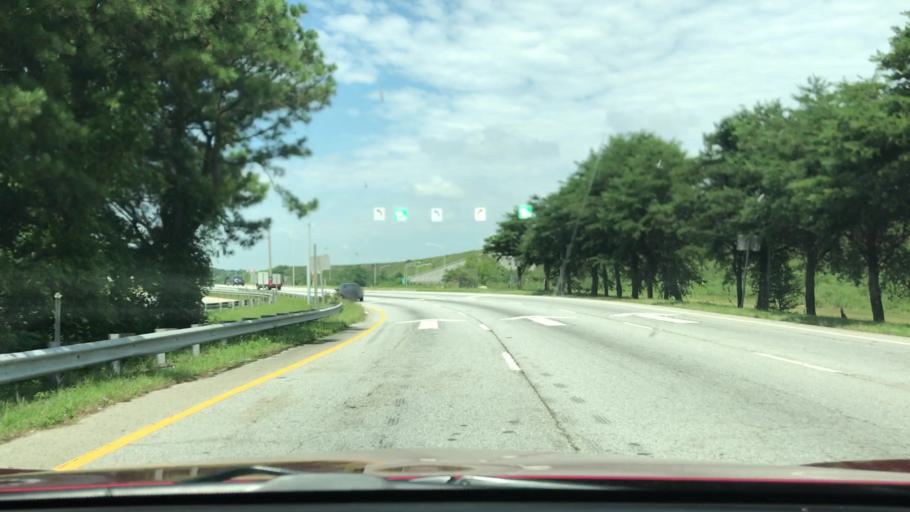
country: US
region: Georgia
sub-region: Fulton County
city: College Park
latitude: 33.6186
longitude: -84.4370
